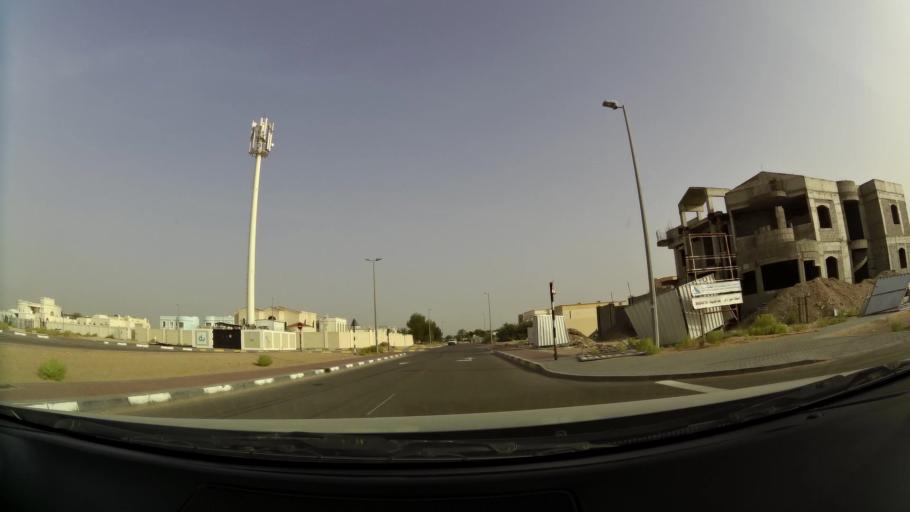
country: AE
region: Abu Dhabi
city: Al Ain
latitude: 24.1276
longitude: 55.6992
